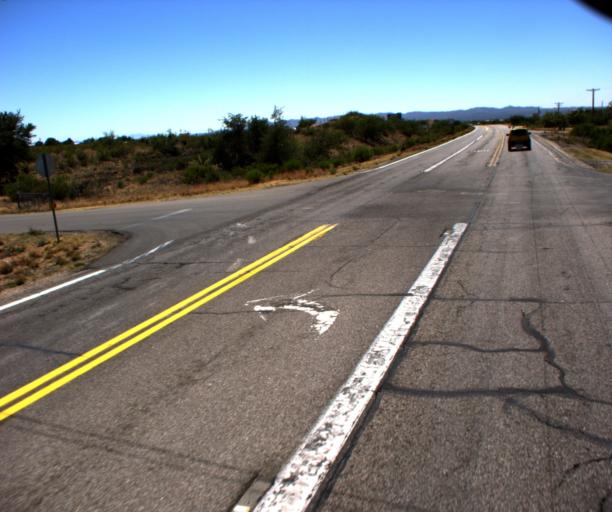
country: US
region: Arizona
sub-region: Pinal County
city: Oracle
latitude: 32.6222
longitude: -110.7954
